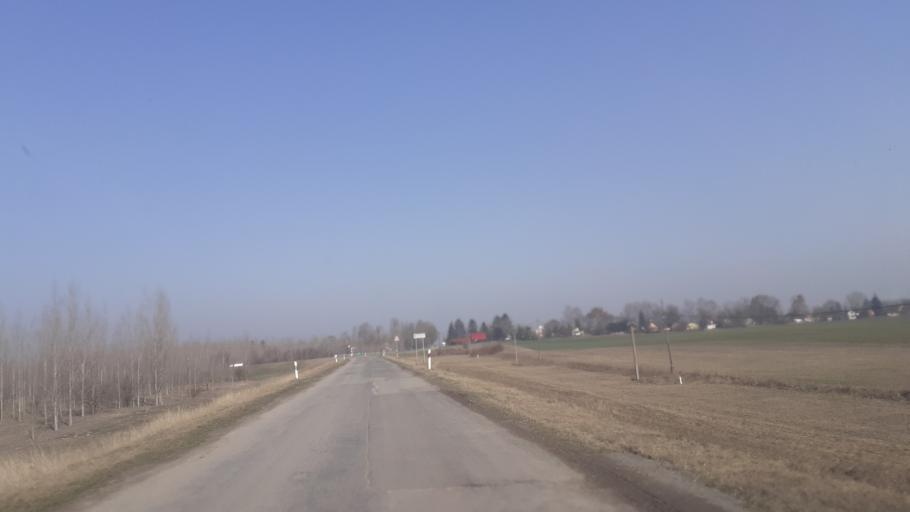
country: HU
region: Fejer
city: Racalmas
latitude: 47.0287
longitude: 18.9838
